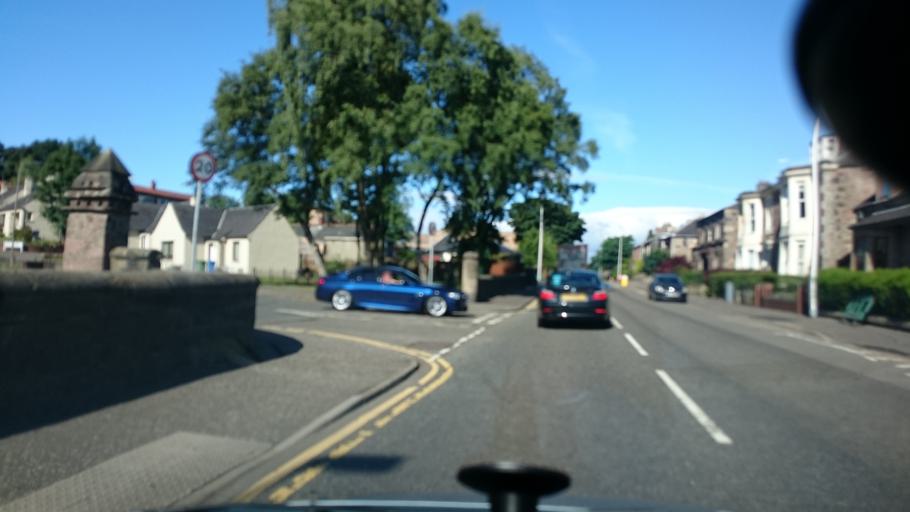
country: GB
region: Scotland
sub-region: Clackmannanshire
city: Alloa
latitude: 56.1163
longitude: -3.7826
